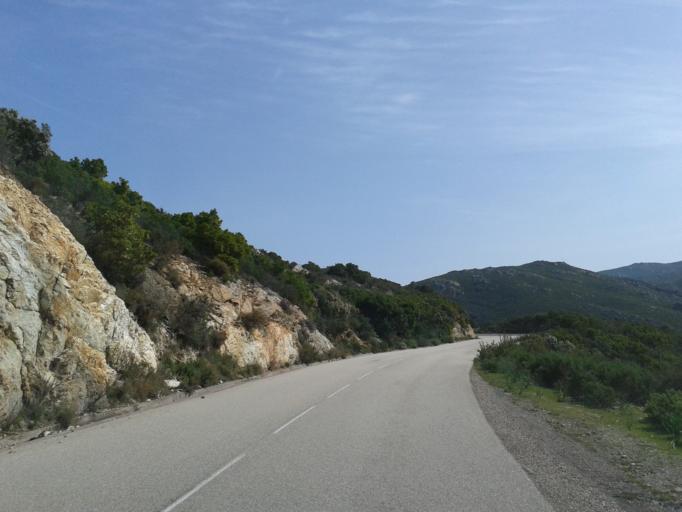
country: FR
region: Corsica
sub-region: Departement de la Haute-Corse
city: Saint-Florent
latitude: 42.6616
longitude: 9.1305
